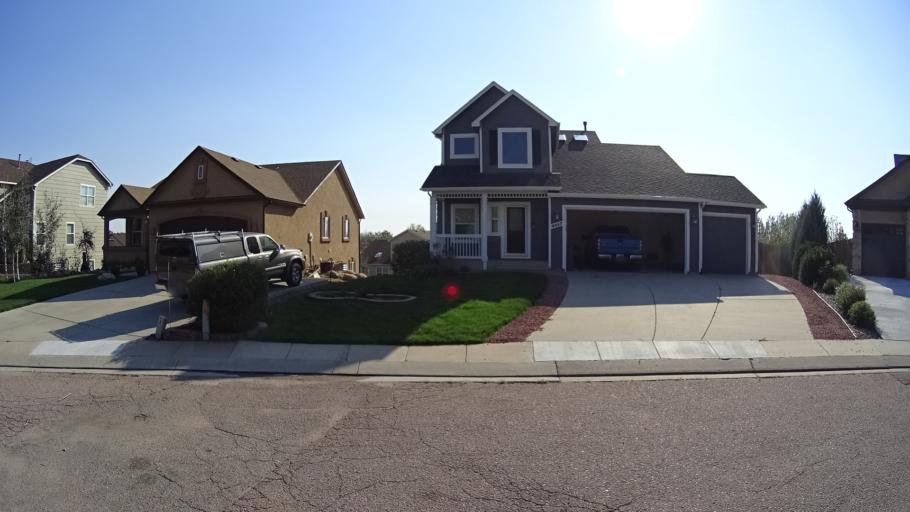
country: US
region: Colorado
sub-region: El Paso County
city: Stratmoor
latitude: 38.7684
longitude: -104.8077
